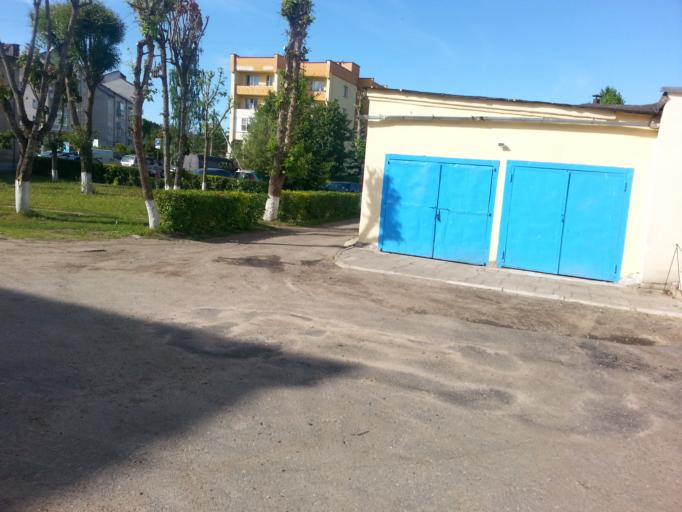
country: BY
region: Minsk
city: Narach
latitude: 54.9091
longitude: 26.7079
